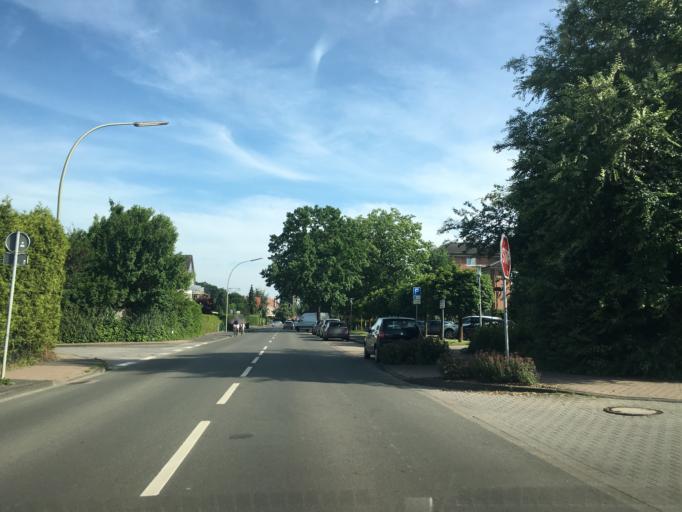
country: DE
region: North Rhine-Westphalia
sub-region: Regierungsbezirk Munster
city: Nordwalde
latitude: 52.0882
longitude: 7.4826
